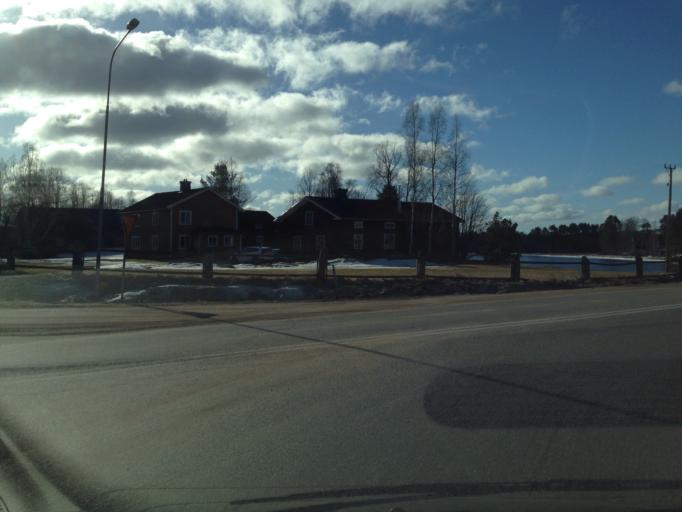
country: SE
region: Jaemtland
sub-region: Harjedalens Kommun
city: Sveg
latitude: 62.0476
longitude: 14.6501
